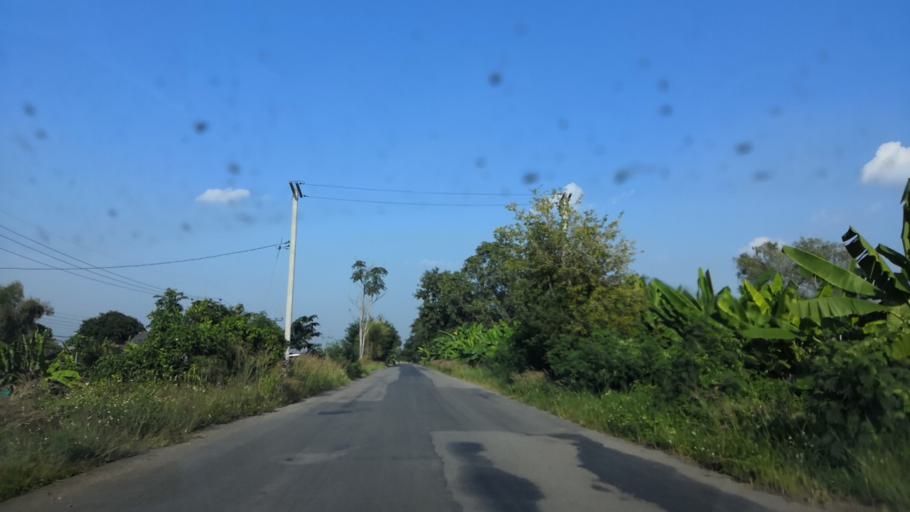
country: TH
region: Chiang Rai
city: Wiang Chai
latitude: 19.9543
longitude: 99.9335
